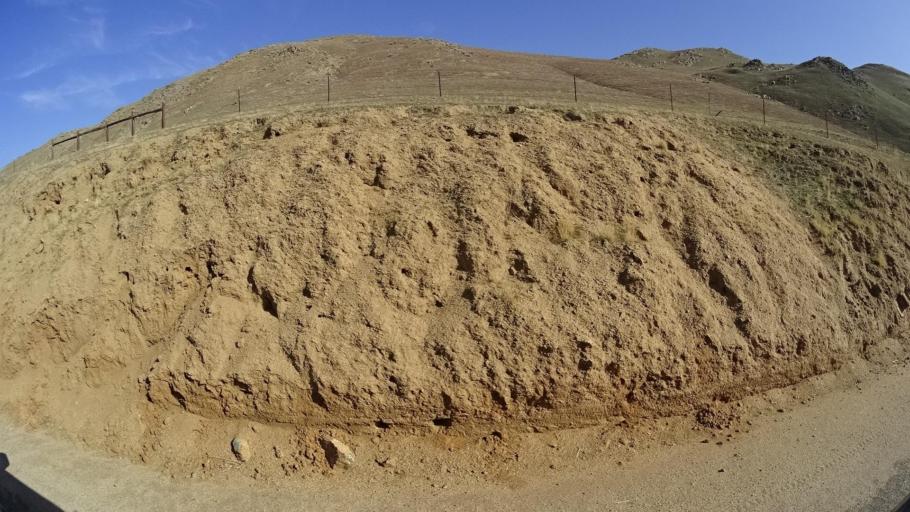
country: US
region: California
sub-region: Kern County
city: Oildale
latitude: 35.4662
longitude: -118.8268
